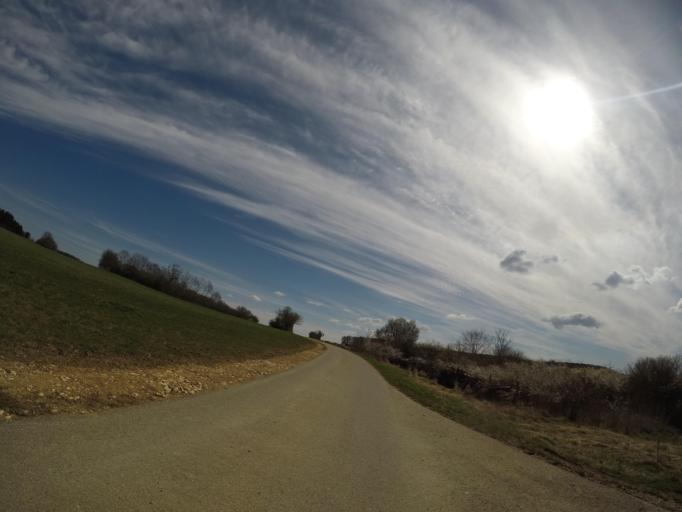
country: DE
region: Baden-Wuerttemberg
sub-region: Tuebingen Region
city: Mehrstetten
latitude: 48.3459
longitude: 9.5918
